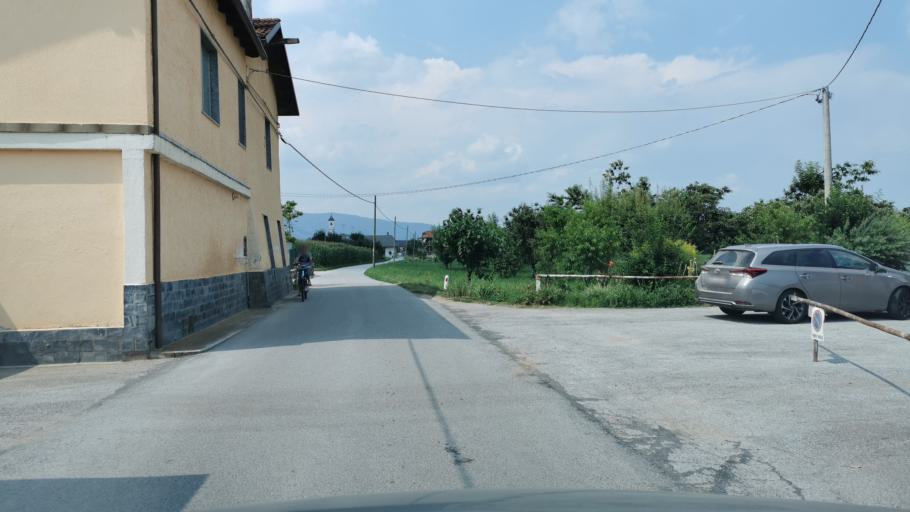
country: IT
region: Piedmont
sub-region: Provincia di Cuneo
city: Caraglio
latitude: 44.4274
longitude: 7.4518
